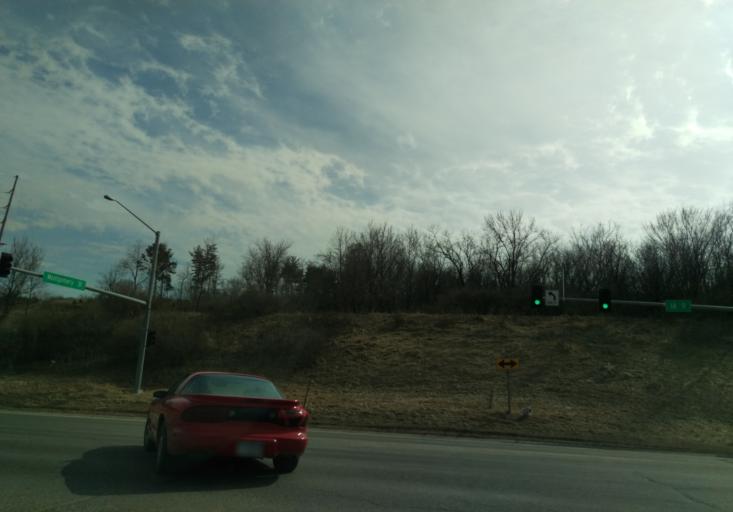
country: US
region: Iowa
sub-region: Winneshiek County
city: Decorah
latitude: 43.2915
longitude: -91.7691
